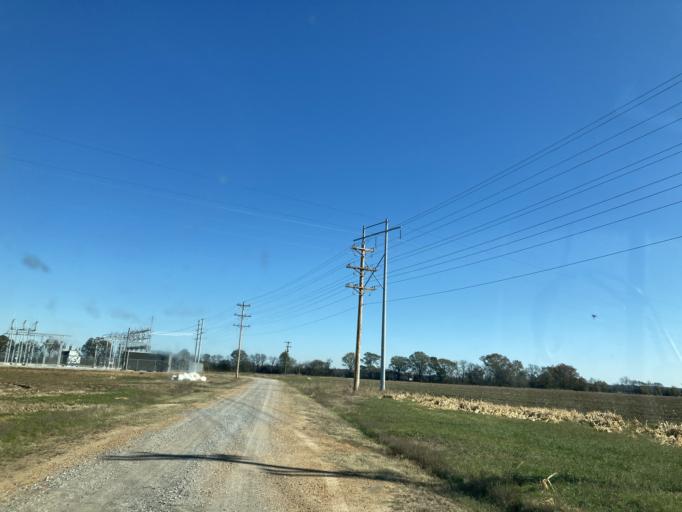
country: US
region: Mississippi
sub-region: Yazoo County
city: Yazoo City
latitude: 32.9157
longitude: -90.4472
